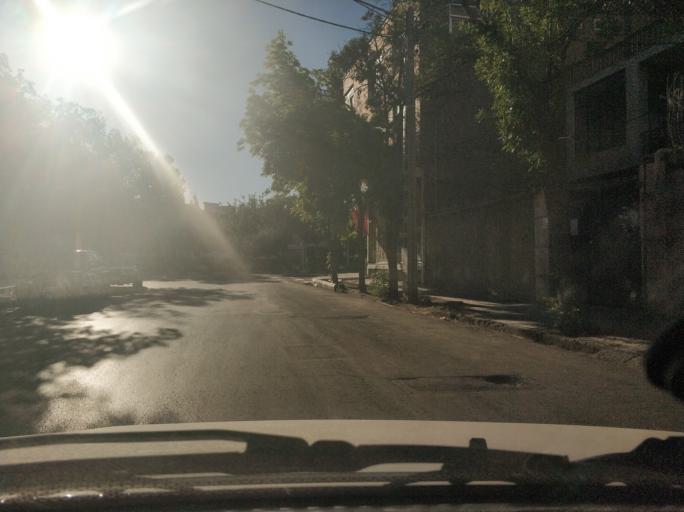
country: IR
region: Razavi Khorasan
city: Mashhad
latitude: 36.2764
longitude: 59.5934
